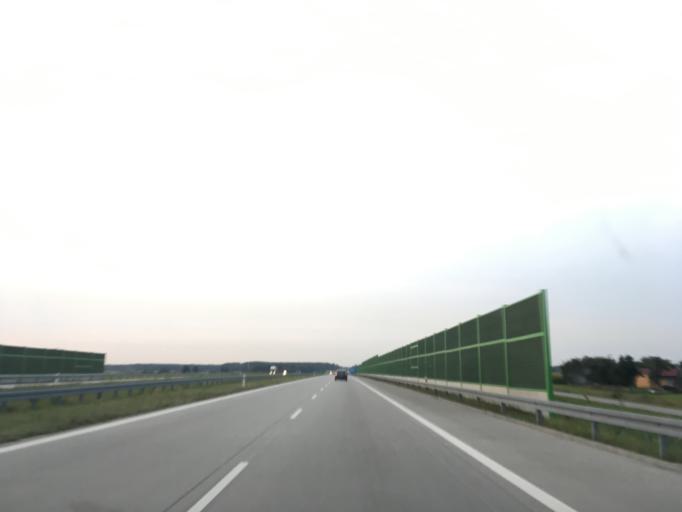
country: PL
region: Lodz Voivodeship
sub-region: Powiat lodzki wschodni
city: Tuszyn
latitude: 51.5784
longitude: 19.5942
